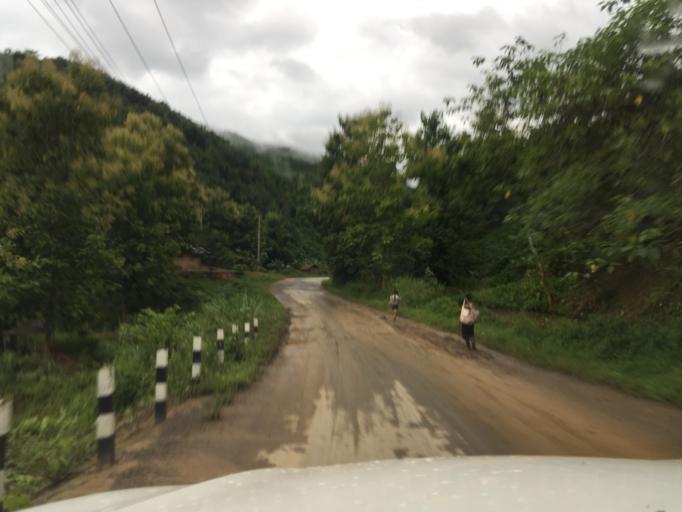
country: LA
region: Oudomxai
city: Muang La
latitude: 20.9773
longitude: 102.2232
